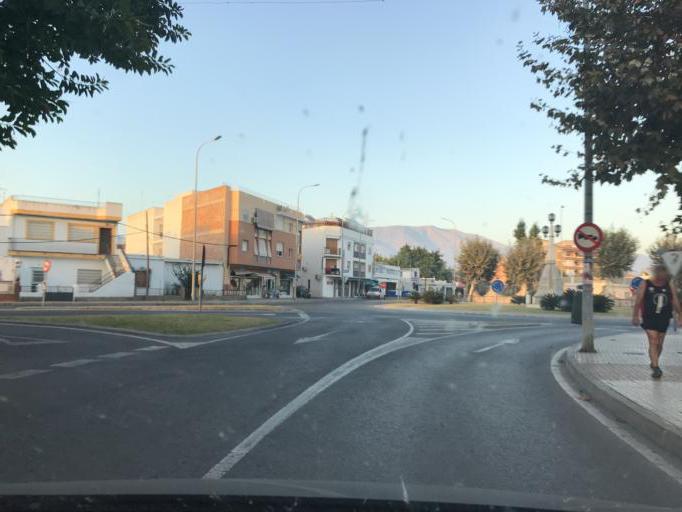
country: ES
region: Andalusia
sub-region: Provincia de Granada
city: El Varadero
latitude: 36.7247
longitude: -3.5325
